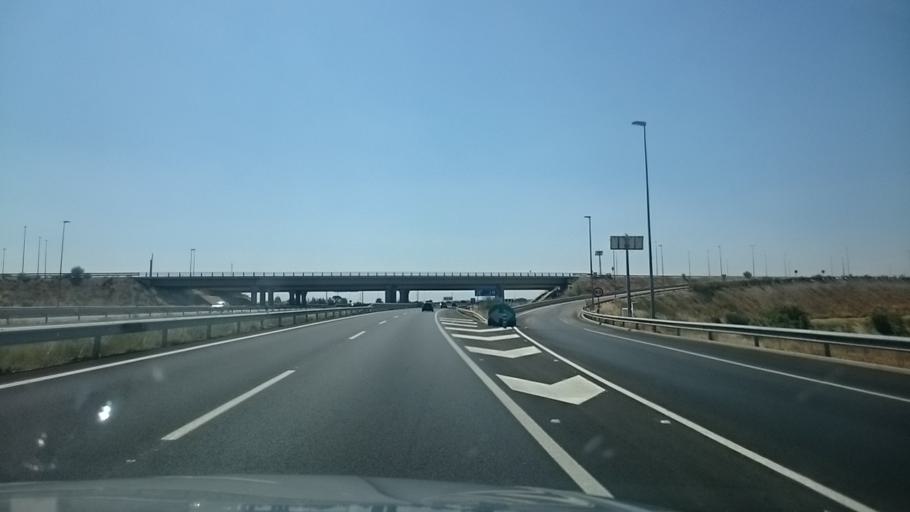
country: ES
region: Aragon
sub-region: Provincia de Zaragoza
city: Nuez de Ebro
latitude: 41.5804
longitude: -0.6635
